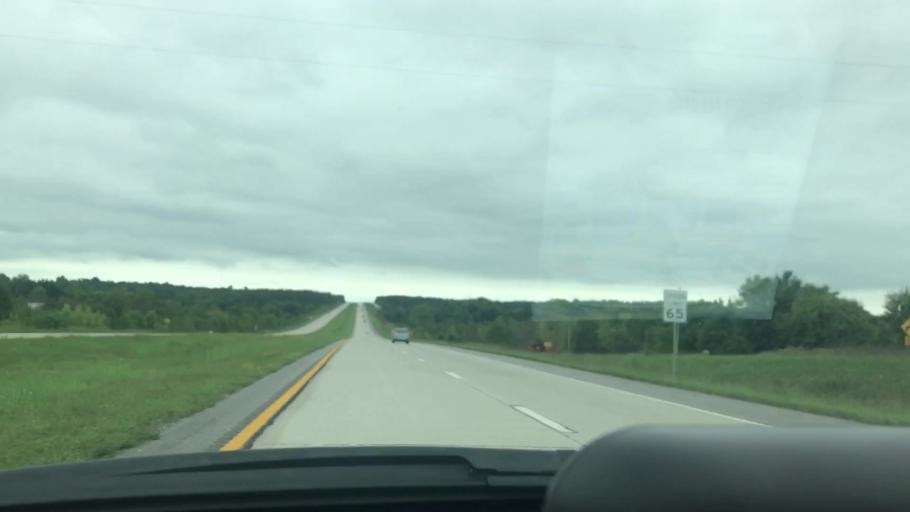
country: US
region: Missouri
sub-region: Greene County
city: Fair Grove
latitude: 37.4632
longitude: -93.1390
